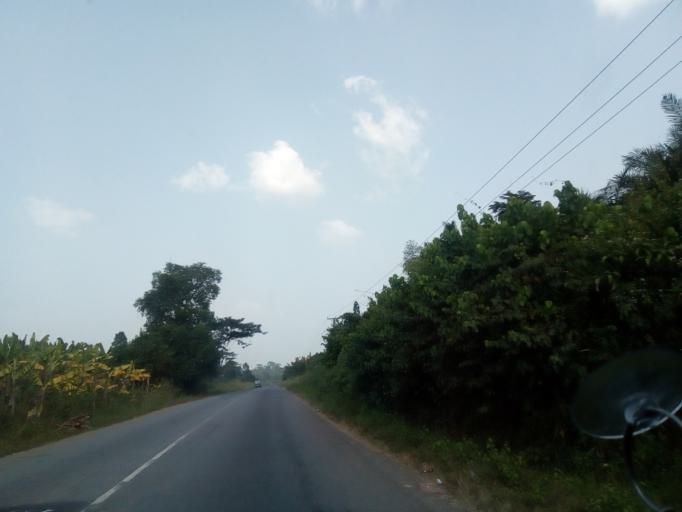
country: GH
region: Eastern
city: Suhum
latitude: 6.0485
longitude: -0.4103
